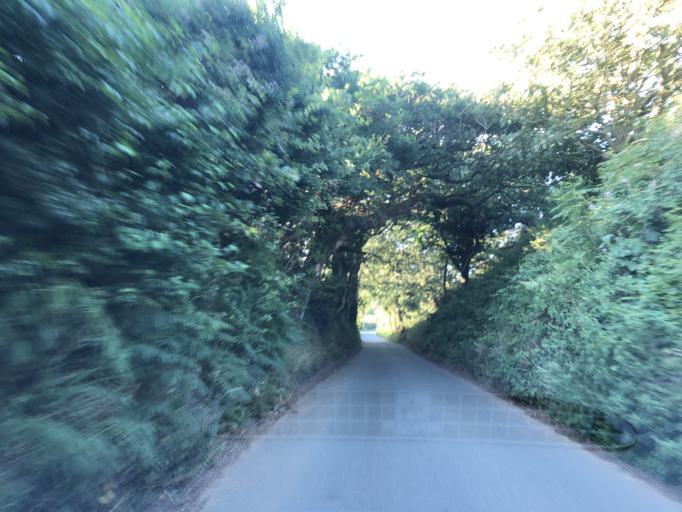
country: GB
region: England
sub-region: Isle of Wight
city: Chale
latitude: 50.6391
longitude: -1.3560
